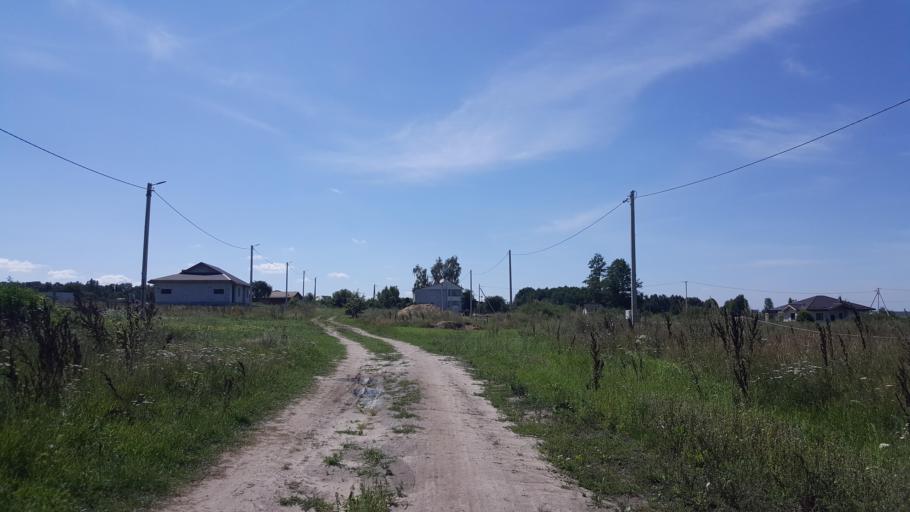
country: BY
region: Brest
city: Charnawchytsy
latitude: 52.2677
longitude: 23.7595
